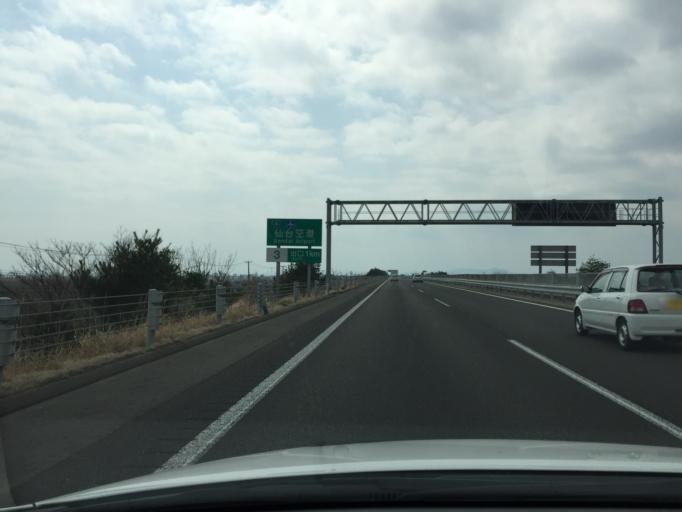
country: JP
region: Miyagi
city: Iwanuma
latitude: 38.1457
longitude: 140.8926
